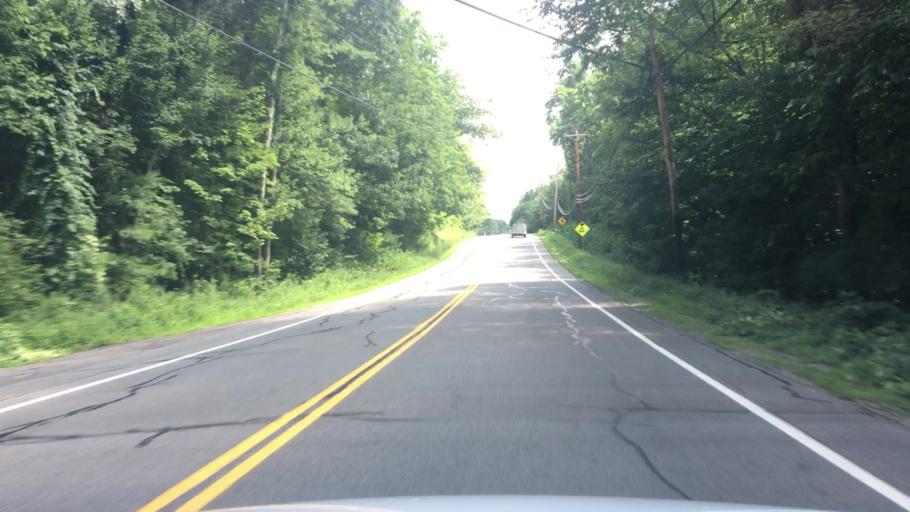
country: US
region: New Hampshire
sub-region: Rockingham County
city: Derry Village
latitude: 42.9356
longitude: -71.3427
